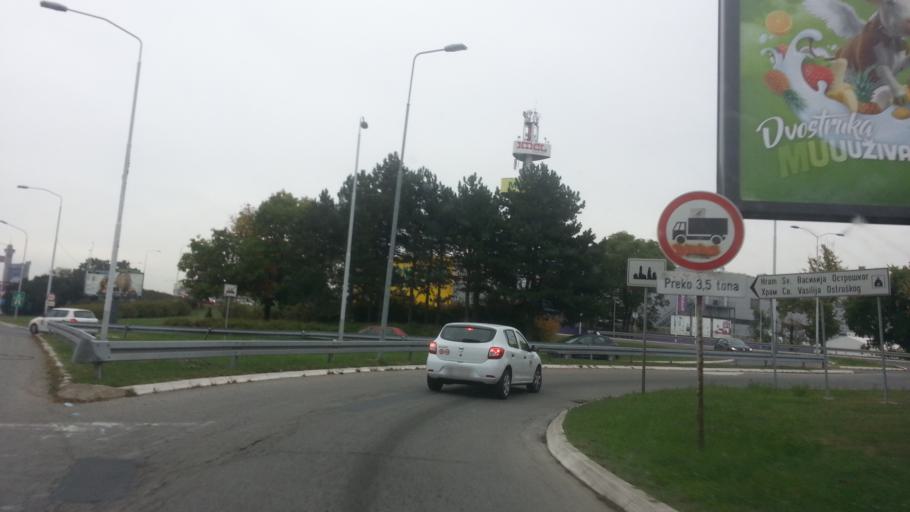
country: RS
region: Central Serbia
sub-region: Belgrade
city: Zemun
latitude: 44.8264
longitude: 20.3891
